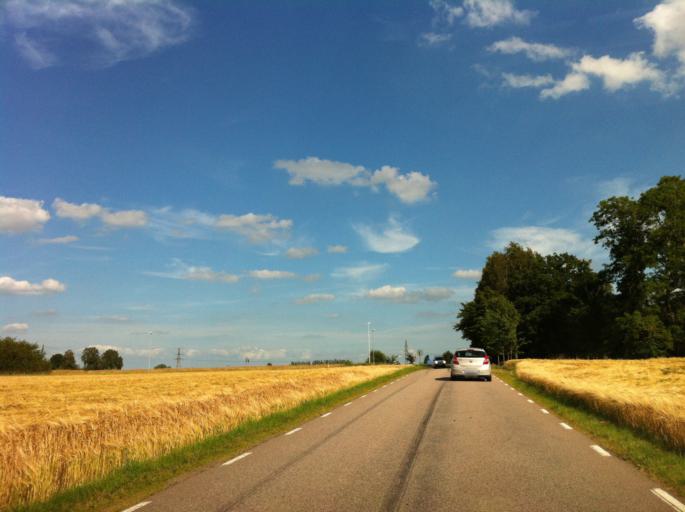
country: SE
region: Skane
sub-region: Helsingborg
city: Barslov
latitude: 55.9765
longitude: 12.8692
